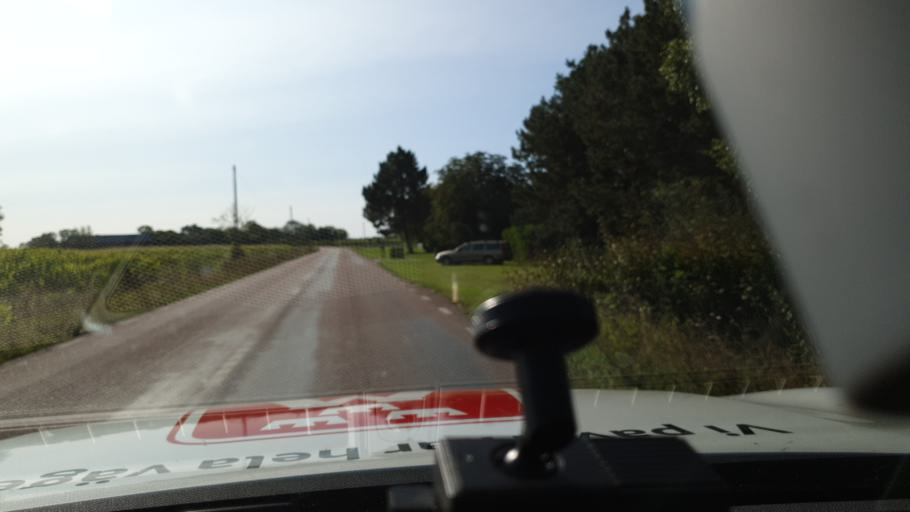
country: SE
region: Gotland
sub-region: Gotland
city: Hemse
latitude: 57.1553
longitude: 18.2812
